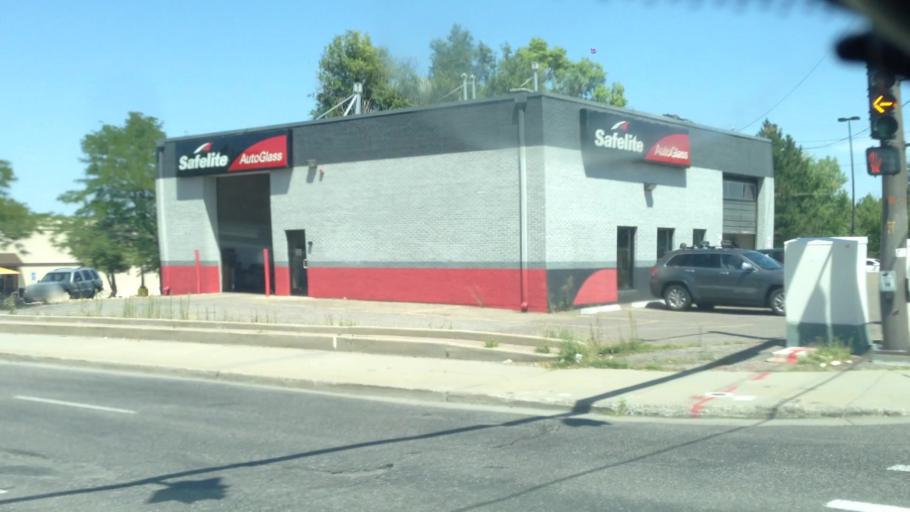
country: US
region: Colorado
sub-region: Jefferson County
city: Lakewood
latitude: 39.7185
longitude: -105.0816
